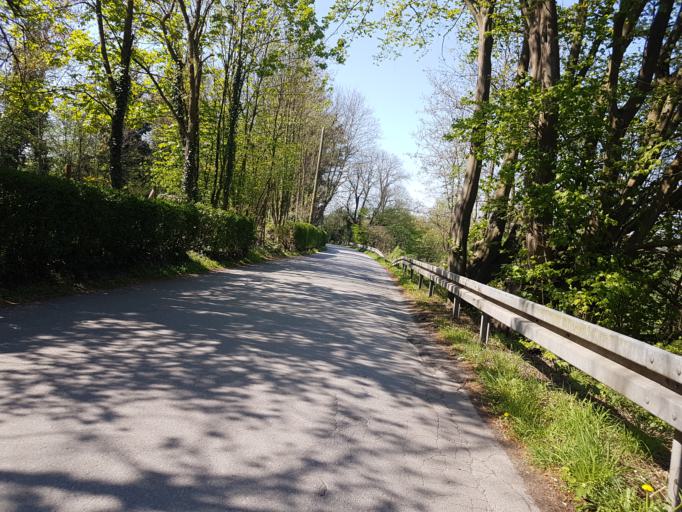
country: DE
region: North Rhine-Westphalia
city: Witten
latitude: 51.4296
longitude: 7.3238
